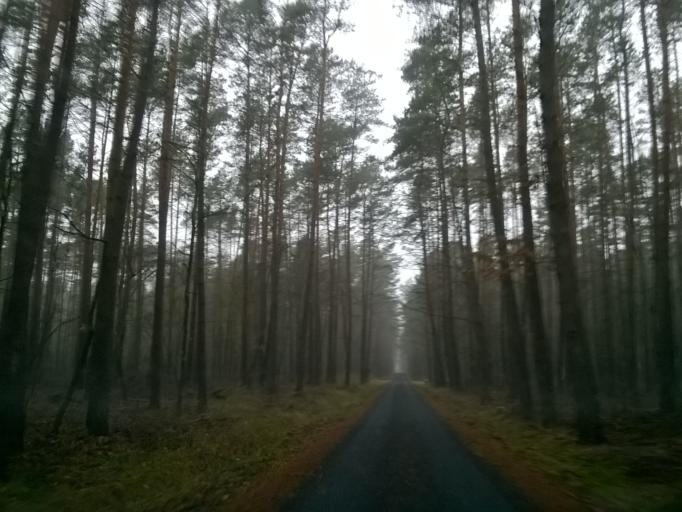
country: PL
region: Kujawsko-Pomorskie
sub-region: Powiat nakielski
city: Kcynia
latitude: 53.0503
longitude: 17.4734
